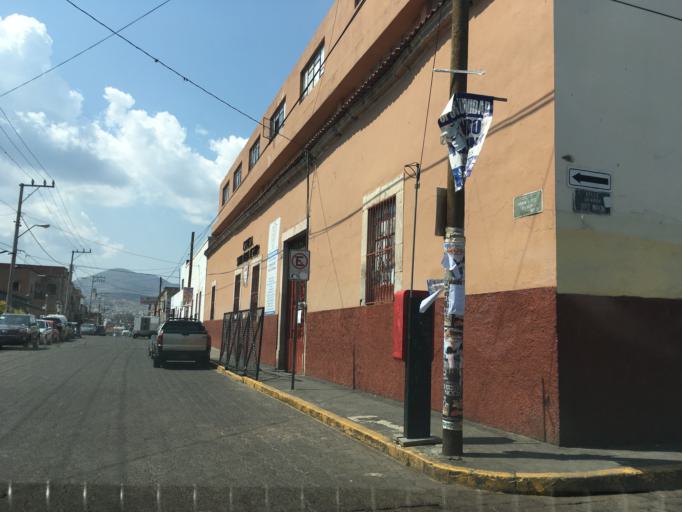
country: MX
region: Michoacan
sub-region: Morelia
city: Montana Monarca (Punta Altozano)
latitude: 19.6734
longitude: -101.1905
